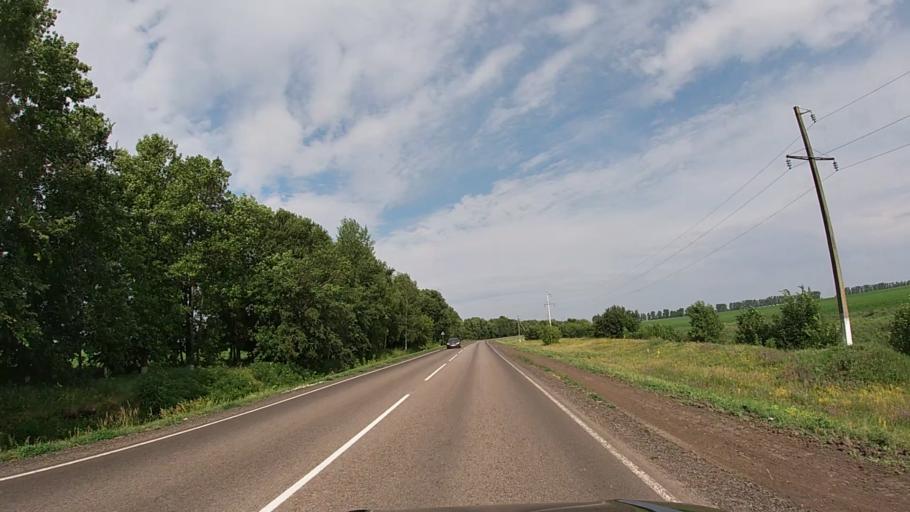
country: RU
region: Belgorod
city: Krasnaya Yaruga
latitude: 50.8014
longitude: 35.5600
